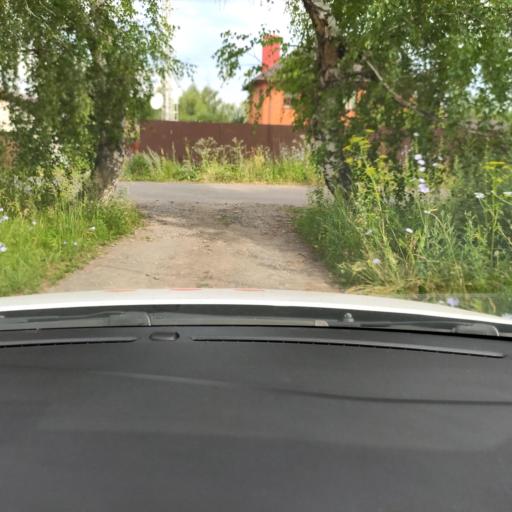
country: RU
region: Tatarstan
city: Stolbishchi
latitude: 55.7599
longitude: 49.2854
